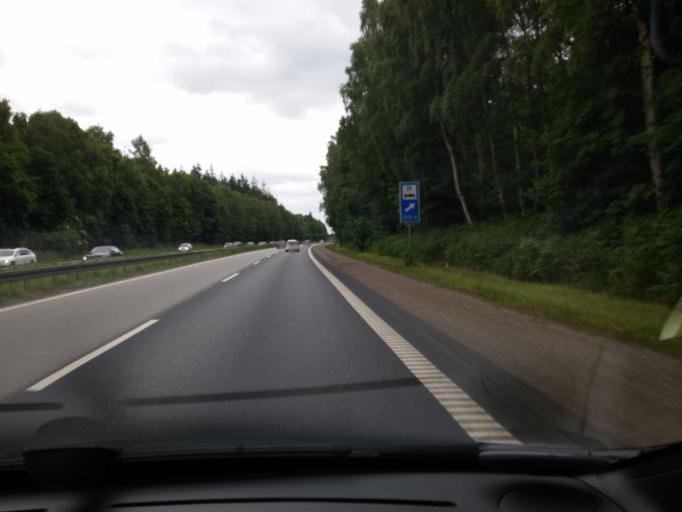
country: DK
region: Capital Region
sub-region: Fureso Kommune
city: Vaerlose
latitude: 55.7895
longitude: 12.3868
